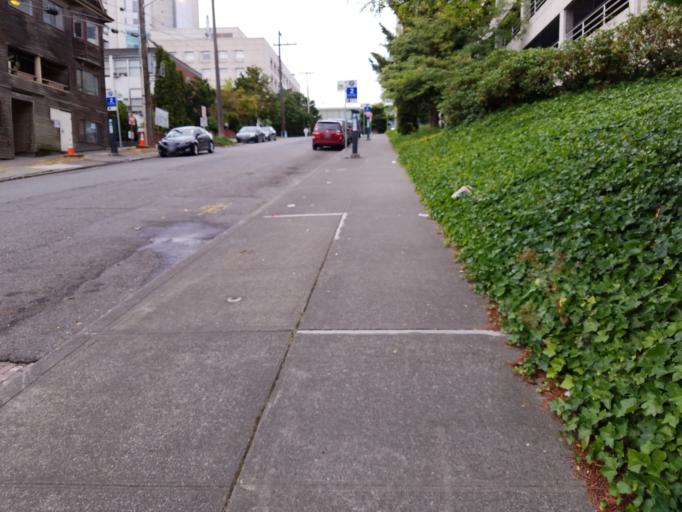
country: US
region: Washington
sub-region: King County
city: Seattle
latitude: 47.6072
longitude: -122.3230
